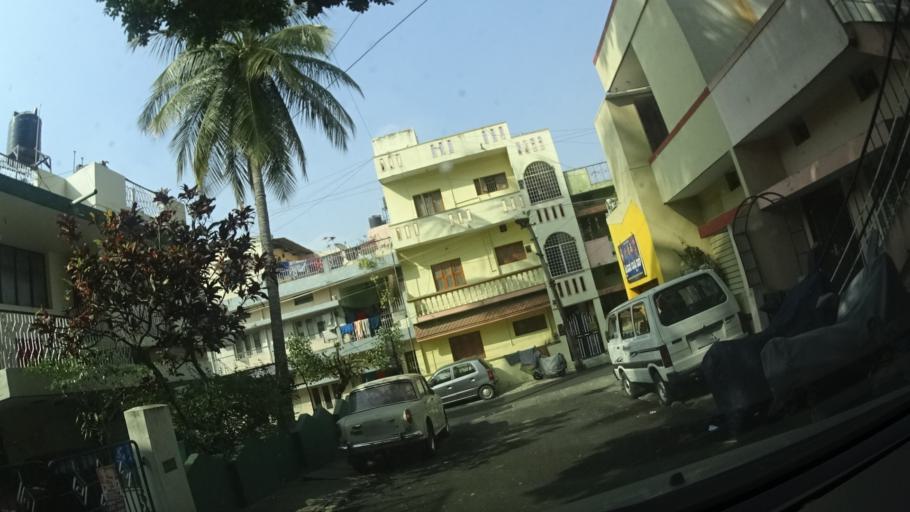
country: IN
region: Karnataka
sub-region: Bangalore Urban
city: Bangalore
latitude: 12.9455
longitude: 77.5603
